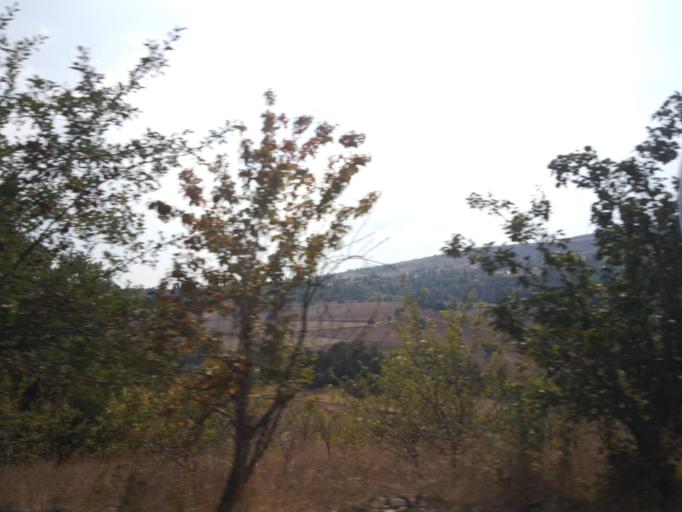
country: TR
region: Tokat
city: Zile
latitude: 40.3708
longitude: 35.8625
